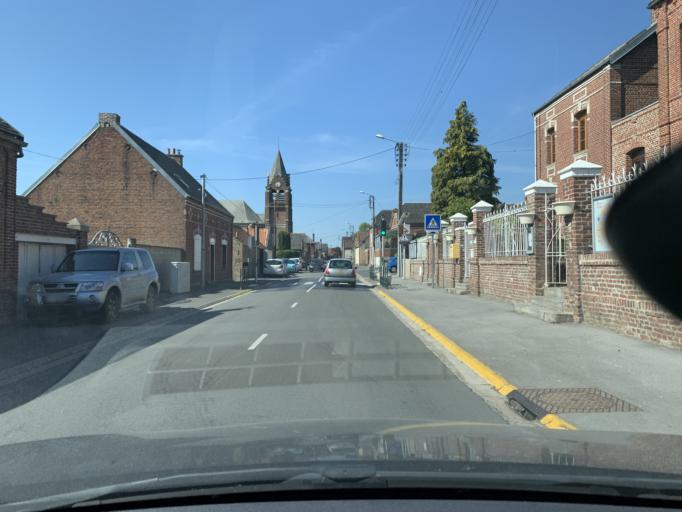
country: FR
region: Nord-Pas-de-Calais
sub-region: Departement du Nord
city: Masnieres
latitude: 50.0964
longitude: 3.2398
